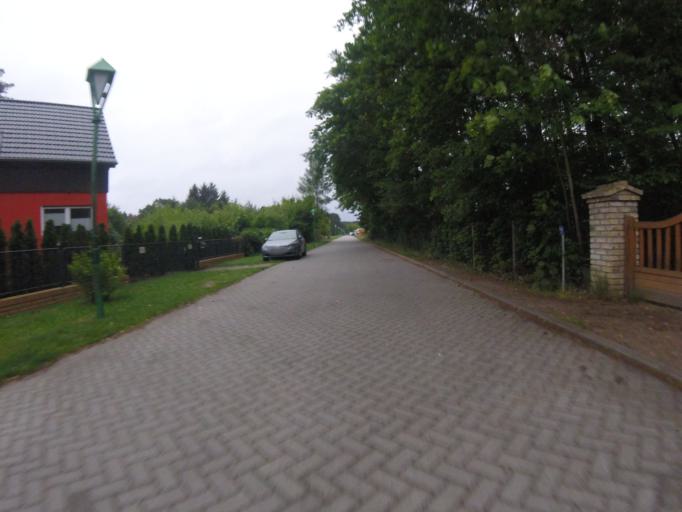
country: DE
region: Brandenburg
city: Bestensee
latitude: 52.2376
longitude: 13.7160
